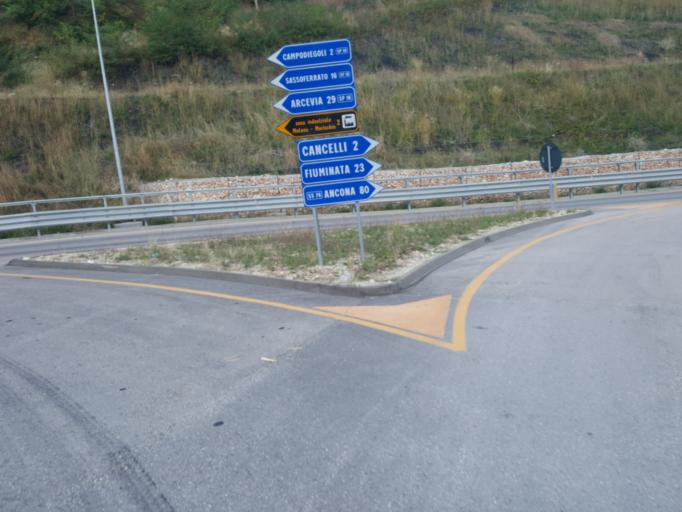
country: IT
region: Umbria
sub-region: Provincia di Perugia
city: Fossato di Vico
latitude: 43.3048
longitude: 12.8252
